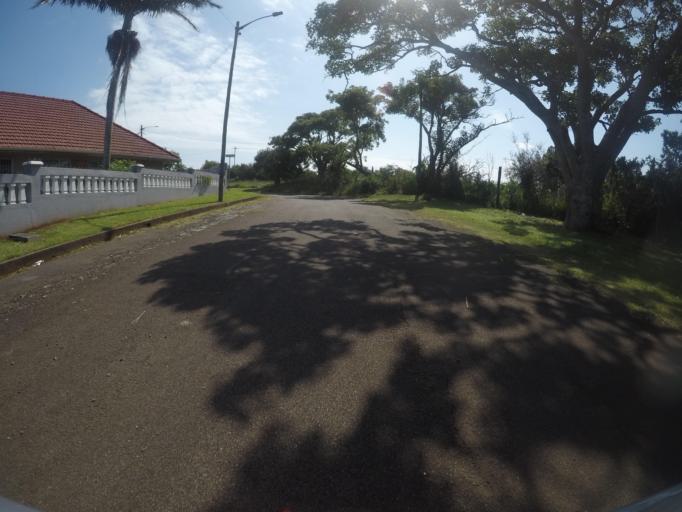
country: ZA
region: Eastern Cape
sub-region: Buffalo City Metropolitan Municipality
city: East London
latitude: -32.9682
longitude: 27.8758
